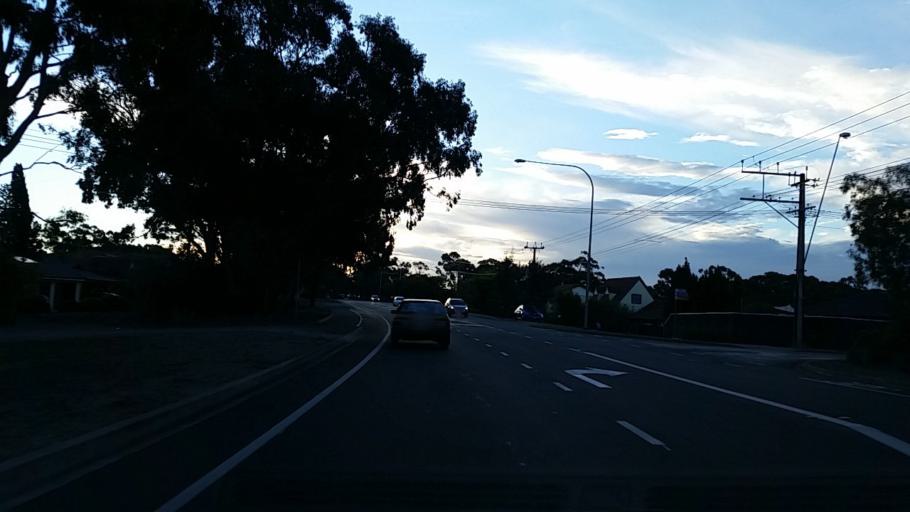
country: AU
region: South Australia
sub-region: Onkaparinga
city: Craigburn Farm
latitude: -35.0522
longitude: 138.5923
